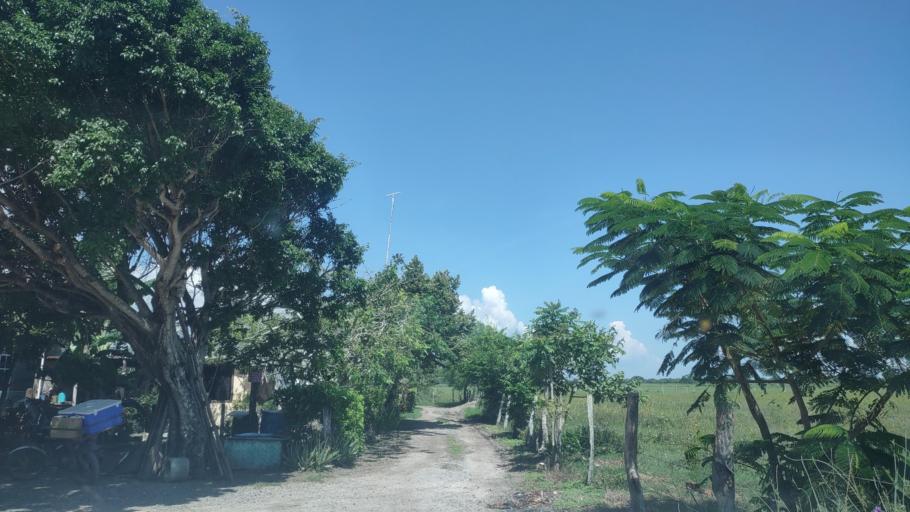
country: MX
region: Veracruz
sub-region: Ozuluama de Mascarenas
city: Cucharas
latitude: 21.6190
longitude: -97.6546
